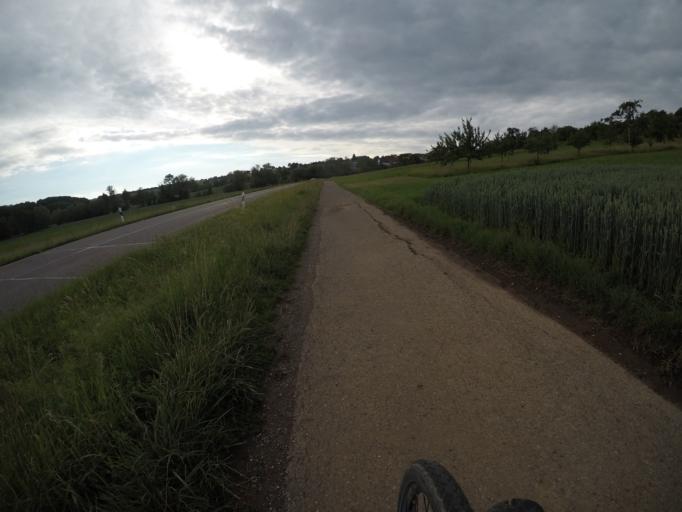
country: DE
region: Baden-Wuerttemberg
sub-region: Regierungsbezirk Stuttgart
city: Schlaitdorf
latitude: 48.5998
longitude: 9.2239
